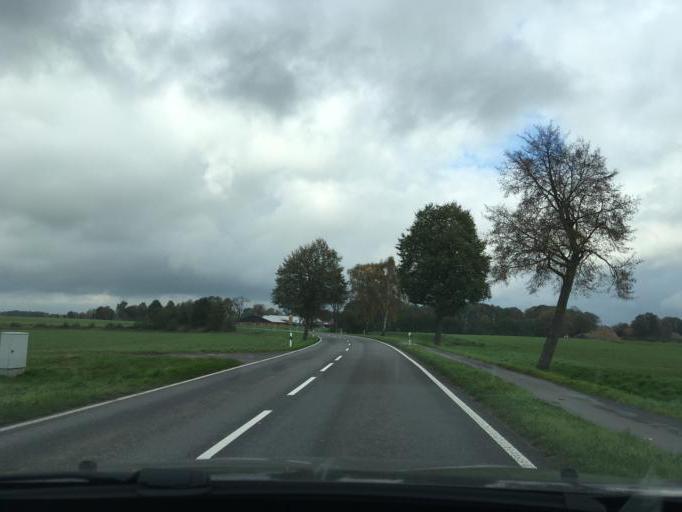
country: DE
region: North Rhine-Westphalia
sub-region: Regierungsbezirk Munster
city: Vreden
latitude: 52.0831
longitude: 6.7805
